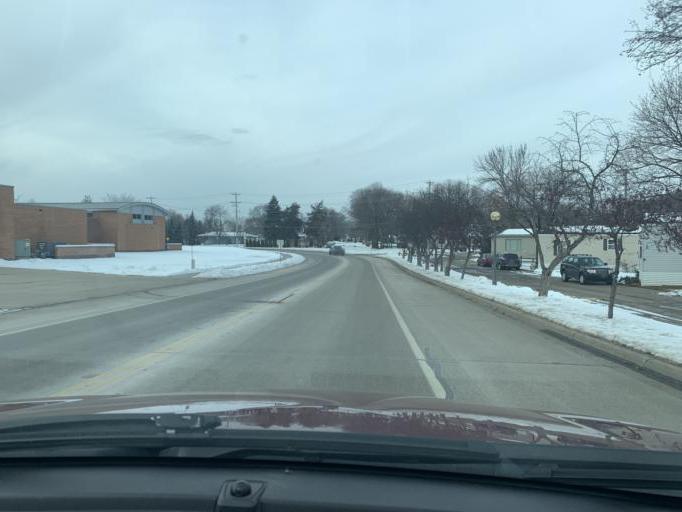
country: US
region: Minnesota
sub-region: Washington County
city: Saint Paul Park
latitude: 44.8471
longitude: -92.9881
